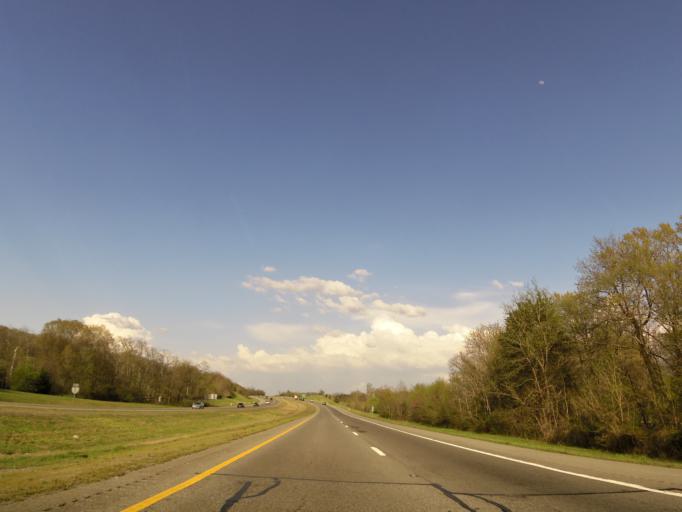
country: US
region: Tennessee
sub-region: Williamson County
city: Nolensville
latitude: 35.8220
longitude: -86.7502
